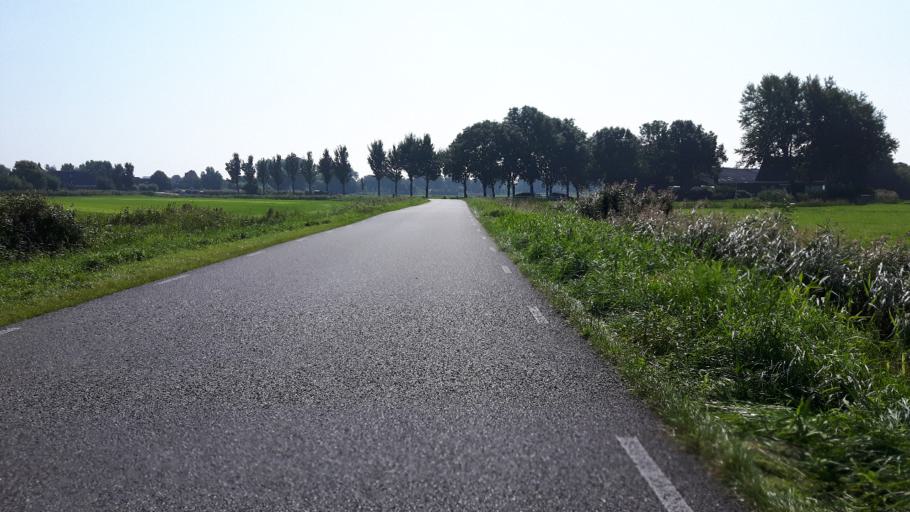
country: NL
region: Friesland
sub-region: Sudwest Fryslan
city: Workum
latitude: 52.9867
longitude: 5.4431
